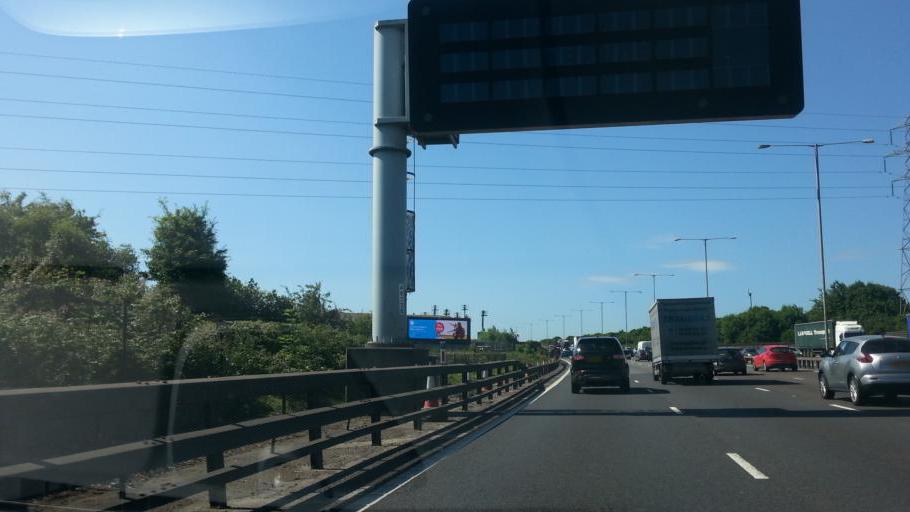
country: GB
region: England
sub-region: Buckinghamshire
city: Iver
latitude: 51.5152
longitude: -0.5006
